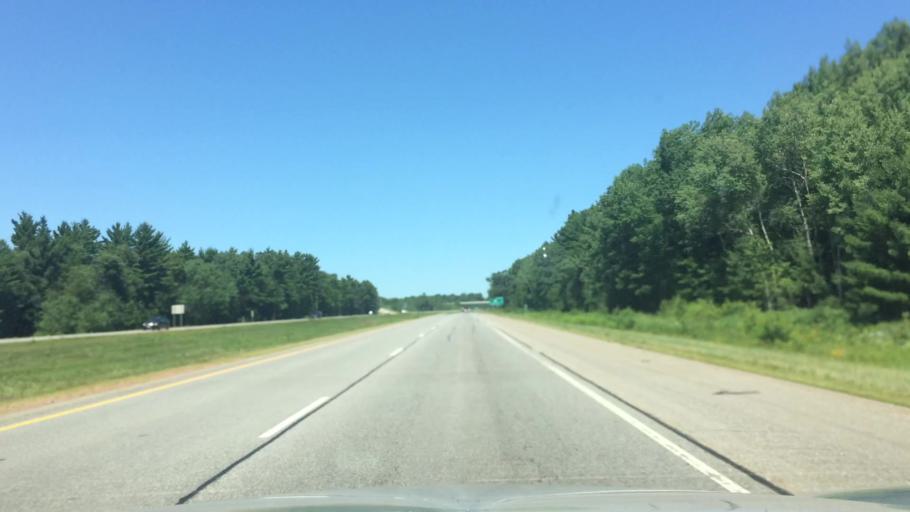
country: US
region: Wisconsin
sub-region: Marathon County
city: Mosinee
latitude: 44.7228
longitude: -89.6705
